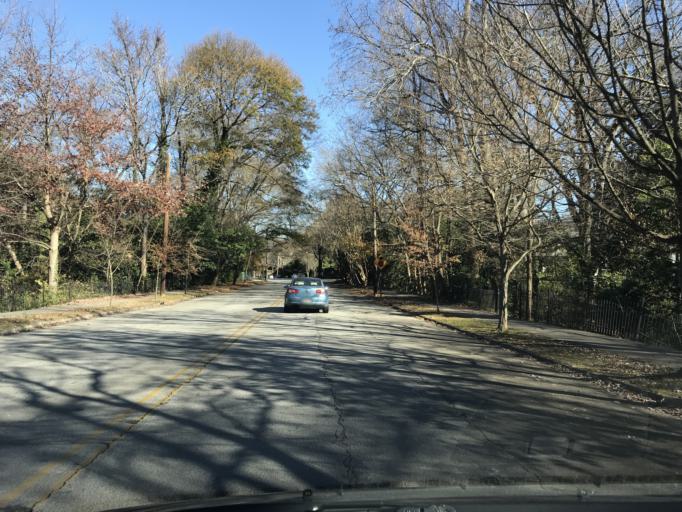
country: US
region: Georgia
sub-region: DeKalb County
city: Druid Hills
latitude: 33.7575
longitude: -84.3574
